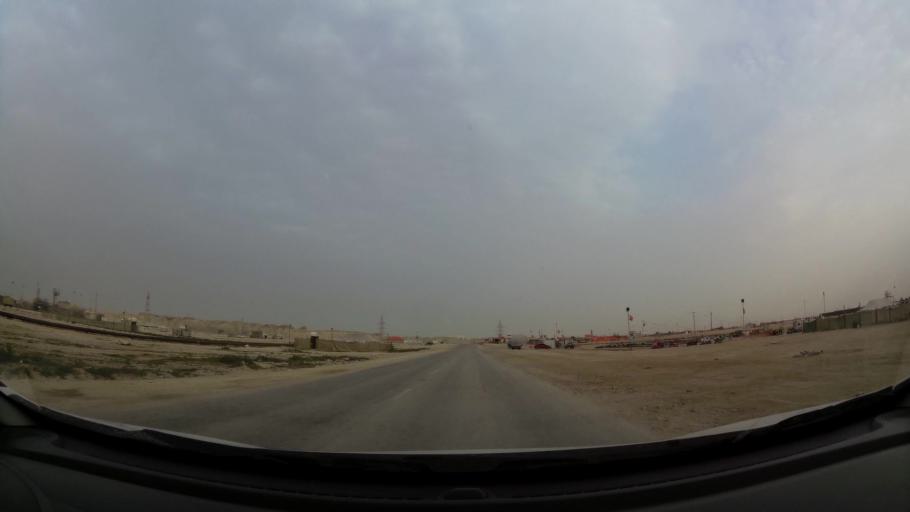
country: BH
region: Central Governorate
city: Dar Kulayb
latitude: 26.0057
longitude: 50.5834
